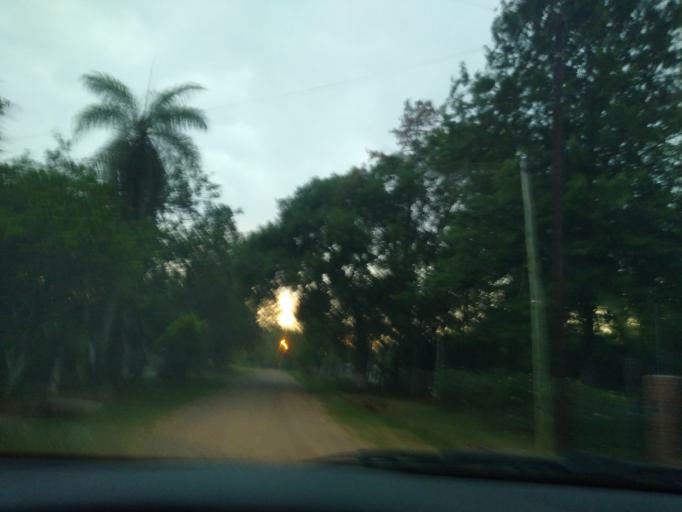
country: AR
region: Chaco
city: Puerto Tirol
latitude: -27.3751
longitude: -59.0847
